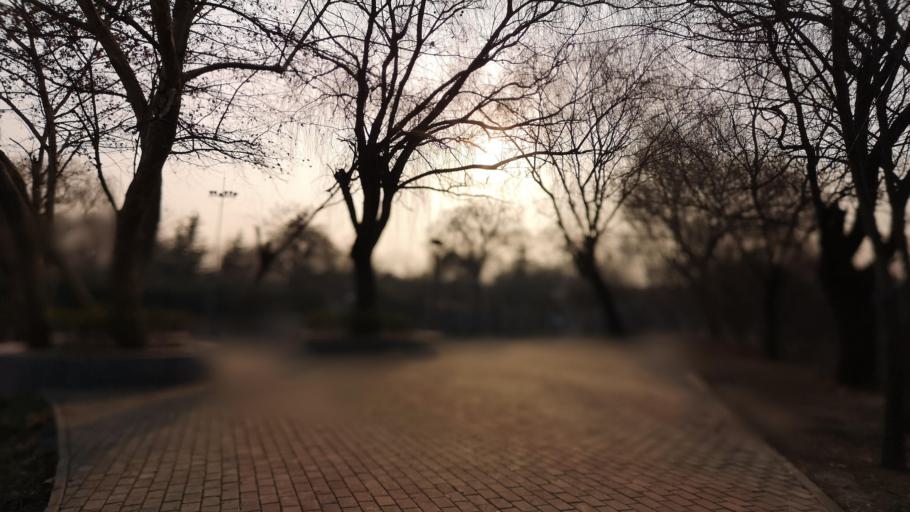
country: CN
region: Henan Sheng
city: Zhongyuanlu
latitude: 35.7456
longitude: 115.0648
